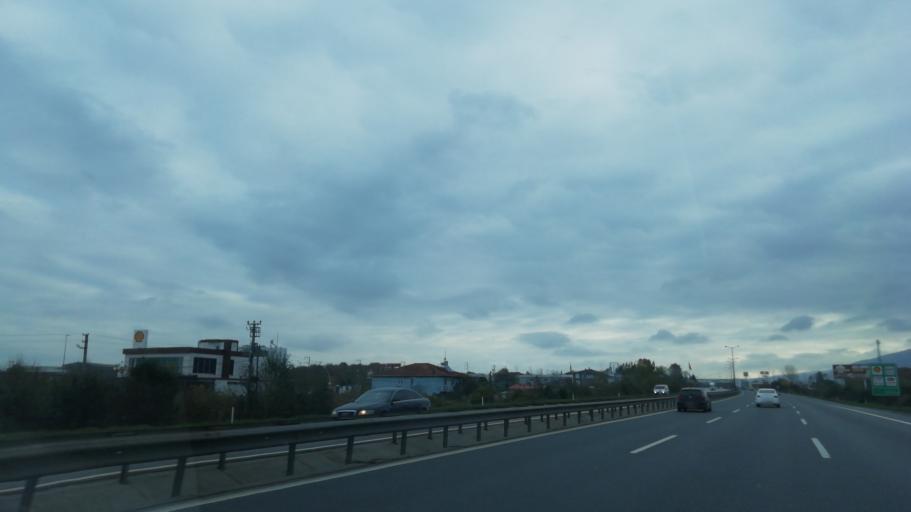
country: TR
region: Kocaeli
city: Derbent
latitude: 40.7303
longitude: 30.0608
